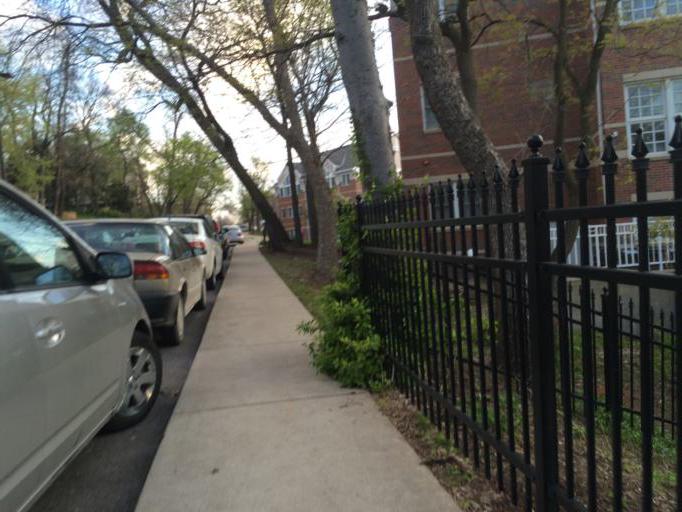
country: US
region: Kansas
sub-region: Douglas County
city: Lawrence
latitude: 38.9586
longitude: -95.2417
